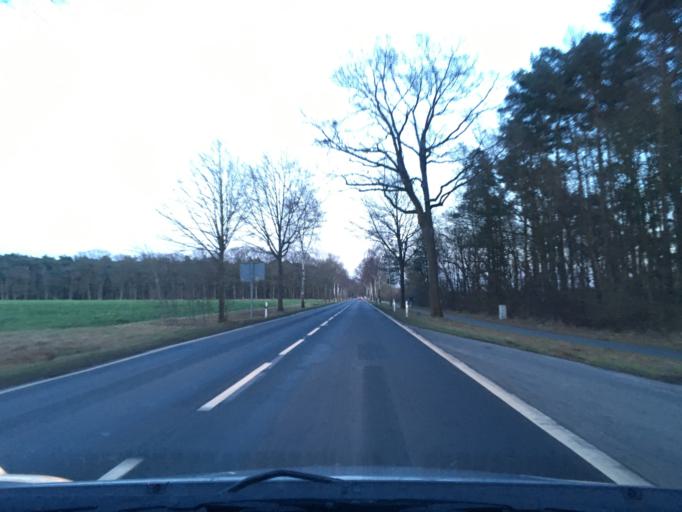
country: DE
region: Lower Saxony
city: Kusten
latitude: 52.9802
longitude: 11.1053
